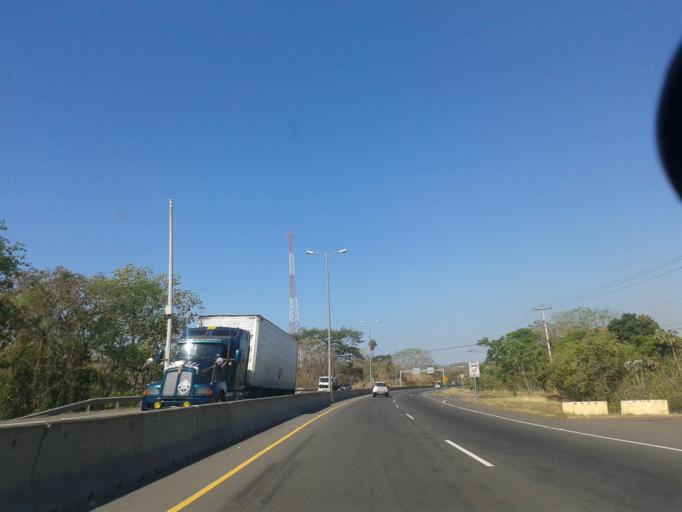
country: CR
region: Alajuela
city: Orotina
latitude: 9.8857
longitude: -84.5829
